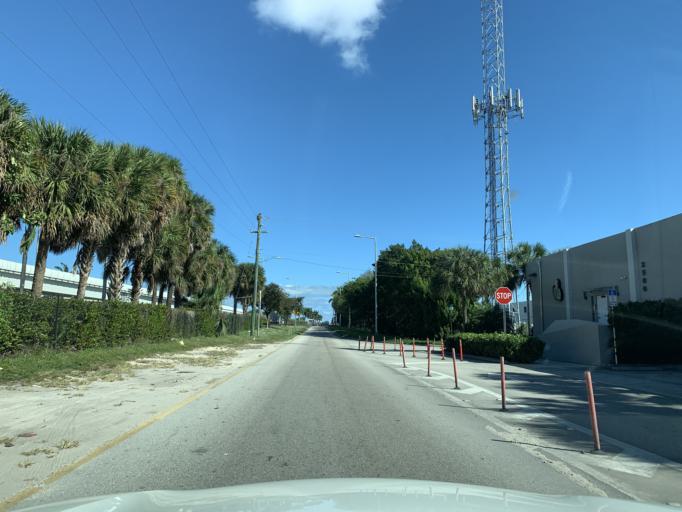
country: US
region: Florida
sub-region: Miami-Dade County
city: Brownsville
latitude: 25.8119
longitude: -80.2388
